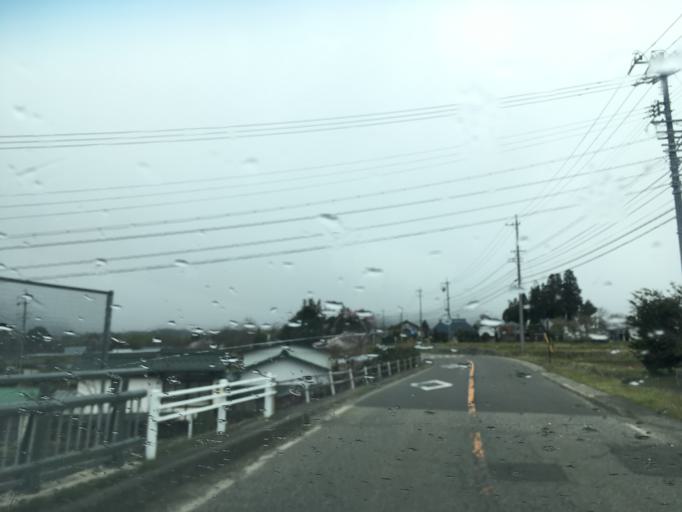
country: JP
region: Nagano
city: Omachi
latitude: 36.5117
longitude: 137.8264
